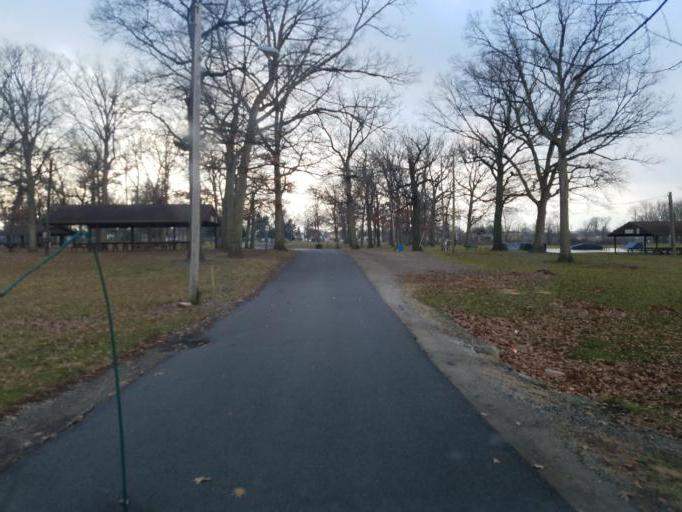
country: US
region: Ohio
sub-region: Marion County
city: Marion
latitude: 40.6035
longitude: -83.1333
